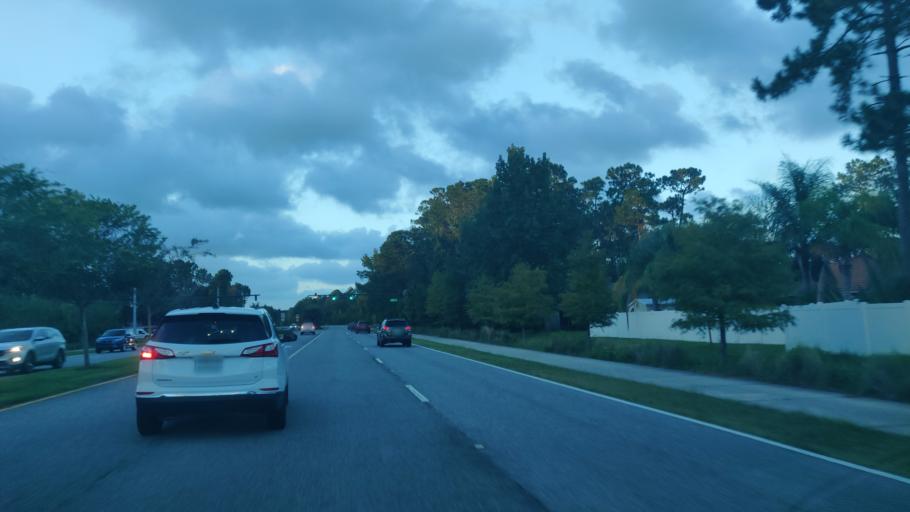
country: US
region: Florida
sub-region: Flagler County
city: Bunnell
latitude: 29.5042
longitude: -81.2198
